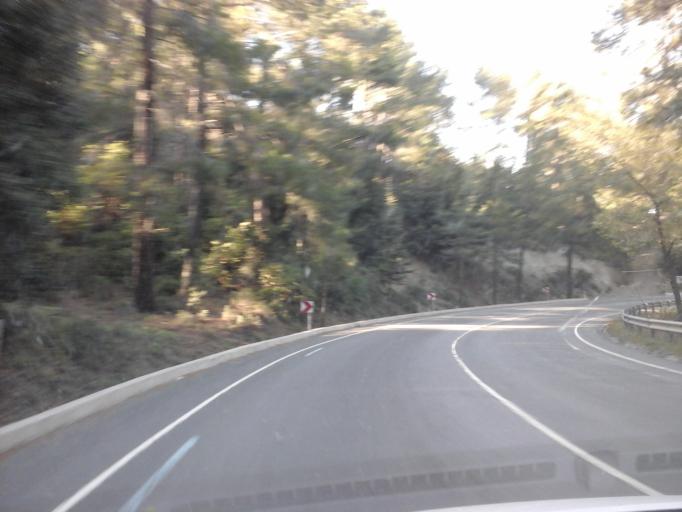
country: CY
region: Lefkosia
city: Kakopetria
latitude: 34.9460
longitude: 32.9260
